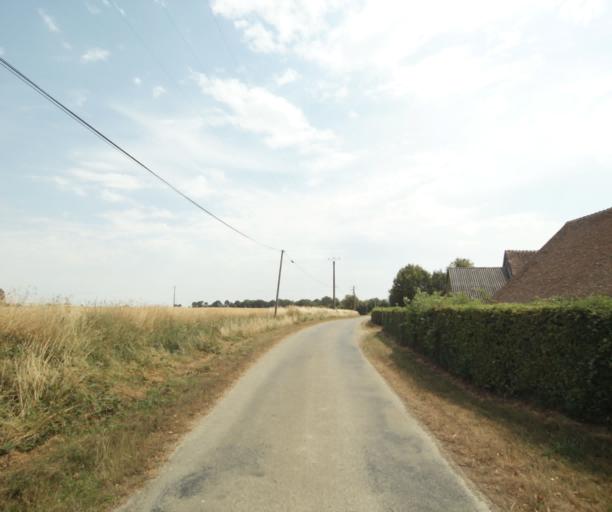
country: FR
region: Centre
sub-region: Departement d'Eure-et-Loir
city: La Bazoche-Gouet
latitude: 48.1877
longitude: 0.9769
